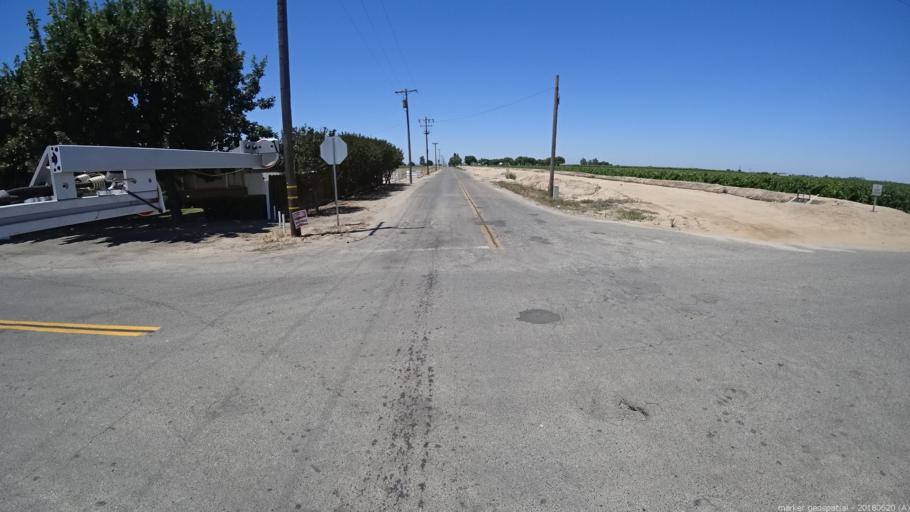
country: US
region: California
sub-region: Fresno County
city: Biola
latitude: 36.8658
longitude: -120.0013
